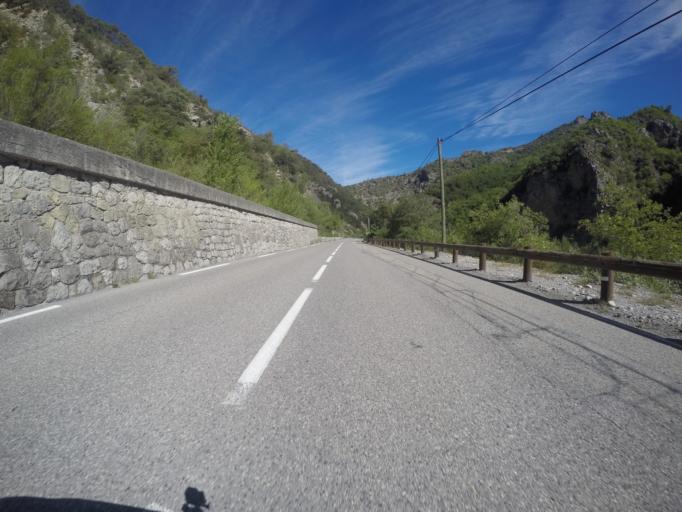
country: FR
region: Provence-Alpes-Cote d'Azur
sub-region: Departement des Alpes-Maritimes
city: Gilette
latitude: 43.9323
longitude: 7.1742
